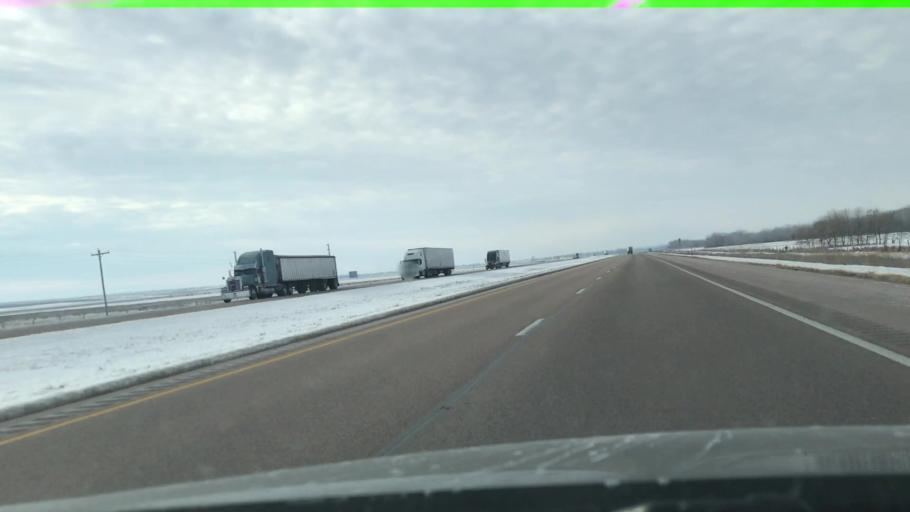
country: US
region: Nebraska
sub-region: Keith County
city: Ogallala
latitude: 41.1199
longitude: -101.6128
